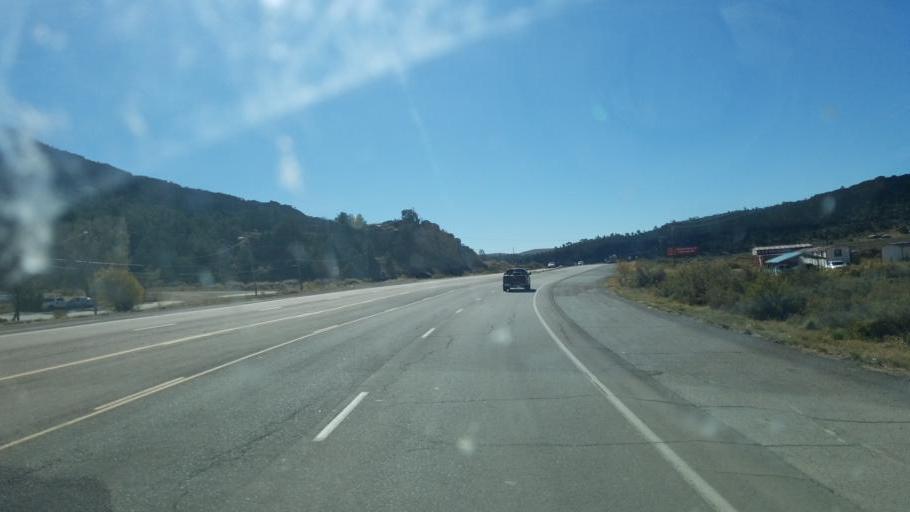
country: US
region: Arizona
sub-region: Apache County
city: Window Rock
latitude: 35.6567
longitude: -109.0400
